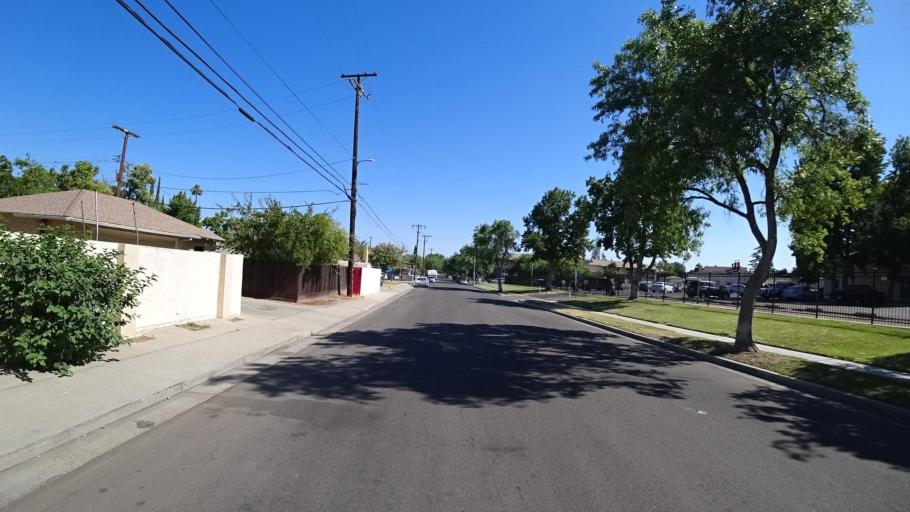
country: US
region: California
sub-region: Fresno County
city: Fresno
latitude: 36.7615
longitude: -119.8199
